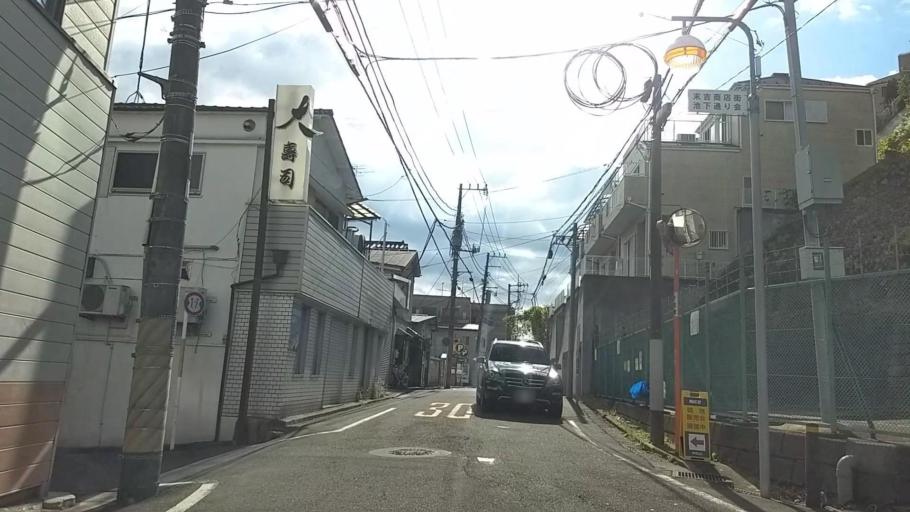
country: JP
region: Kanagawa
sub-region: Kawasaki-shi
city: Kawasaki
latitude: 35.5172
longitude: 139.6708
